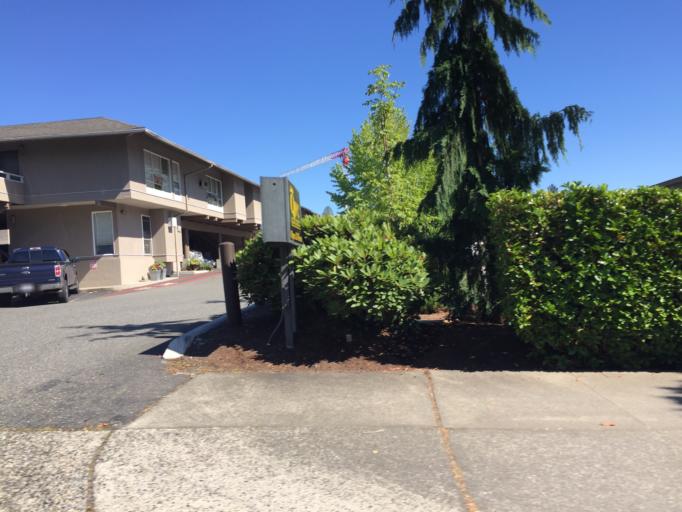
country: US
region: Washington
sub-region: King County
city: Bellevue
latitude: 47.6175
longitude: -122.2061
